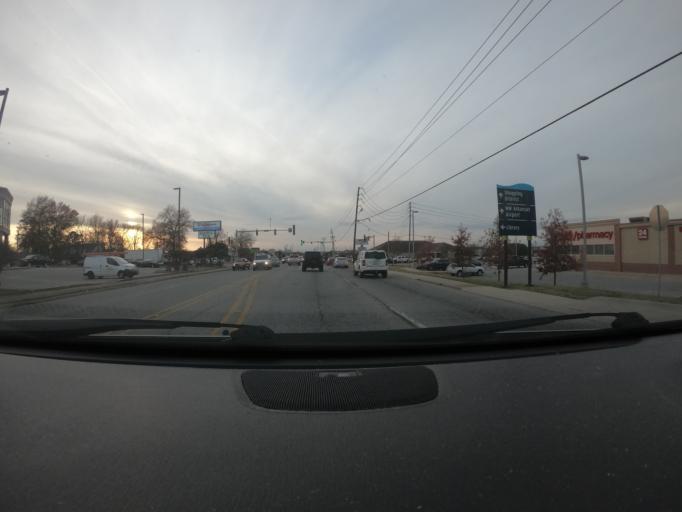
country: US
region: Arkansas
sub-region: Benton County
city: Rogers
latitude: 36.3340
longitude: -94.1427
